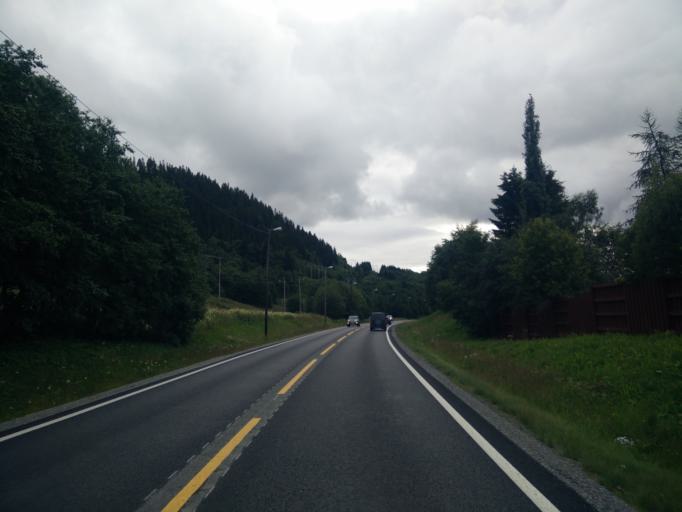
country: NO
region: Sor-Trondelag
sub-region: Orkdal
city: Orkanger
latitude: 63.2828
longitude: 9.8486
